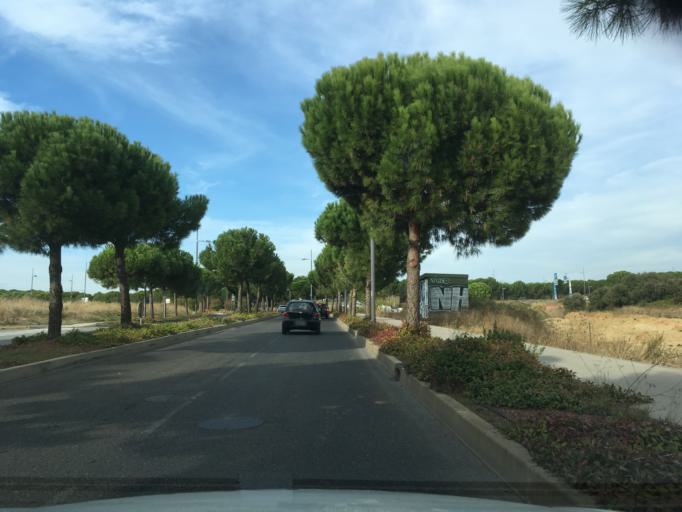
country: FR
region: Languedoc-Roussillon
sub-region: Departement de l'Herault
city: Castelnau-le-Lez
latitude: 43.6060
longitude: 3.9258
